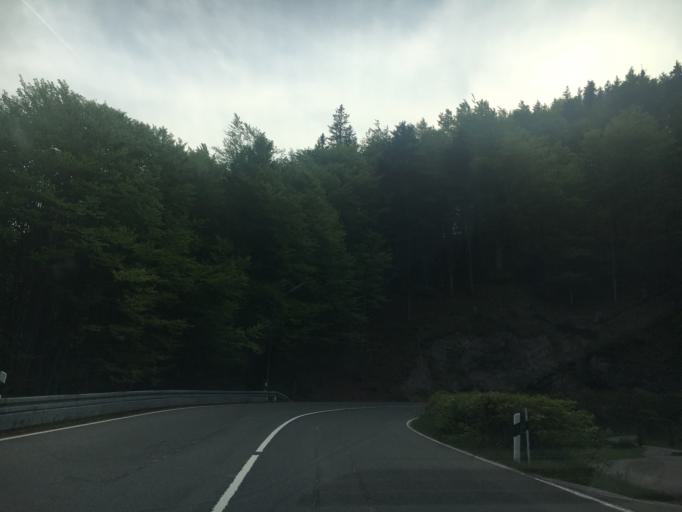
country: DE
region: Bavaria
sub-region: Upper Bavaria
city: Kochel
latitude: 47.6199
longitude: 11.3493
